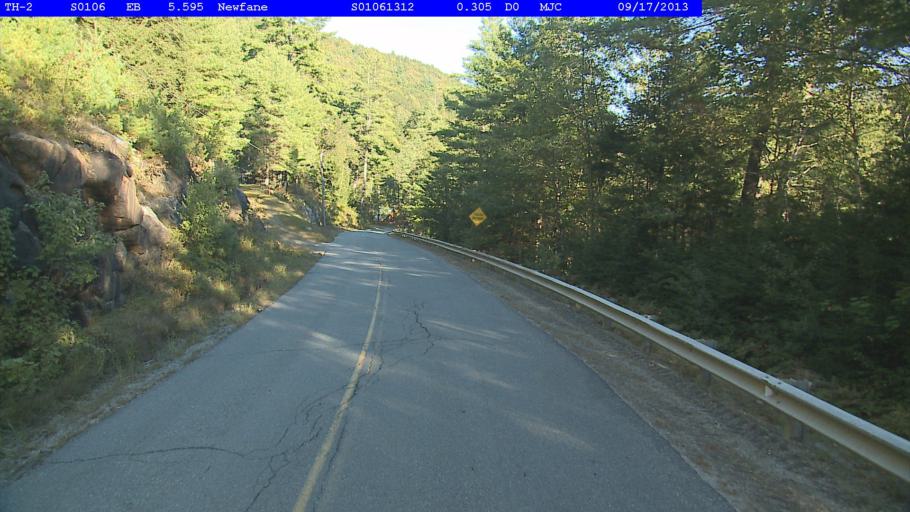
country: US
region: Vermont
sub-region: Windham County
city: Dover
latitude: 42.9498
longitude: -72.7599
